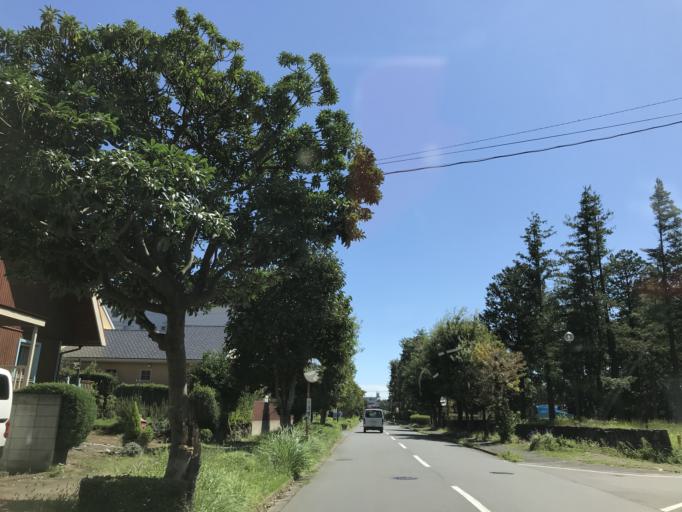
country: JP
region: Ibaraki
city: Tsukuba
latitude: 36.1331
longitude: 140.0847
